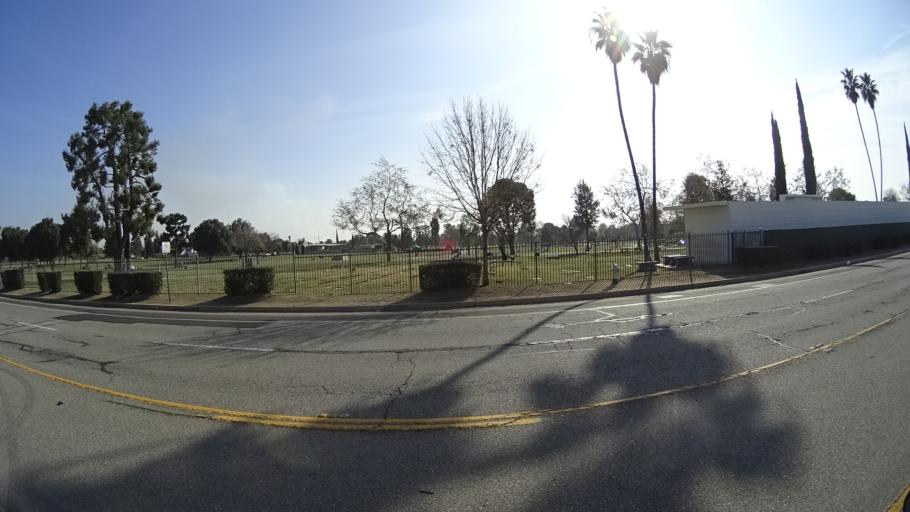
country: US
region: California
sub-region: Kern County
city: Oildale
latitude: 35.4090
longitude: -118.9887
